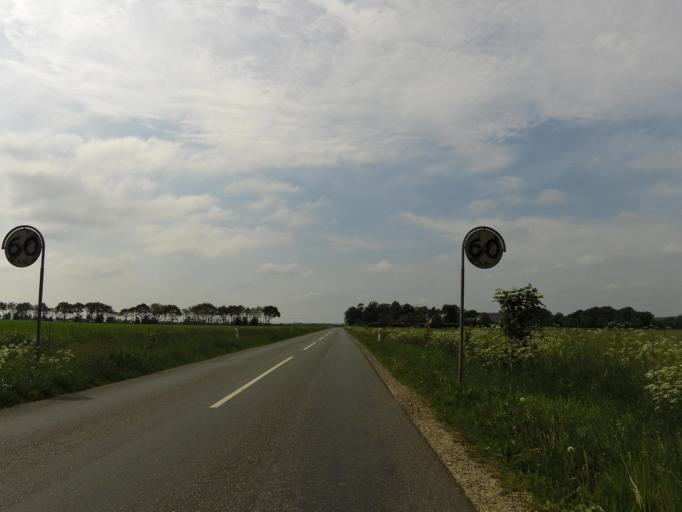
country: DK
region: South Denmark
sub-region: Haderslev Kommune
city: Gram
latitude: 55.2741
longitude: 9.1697
